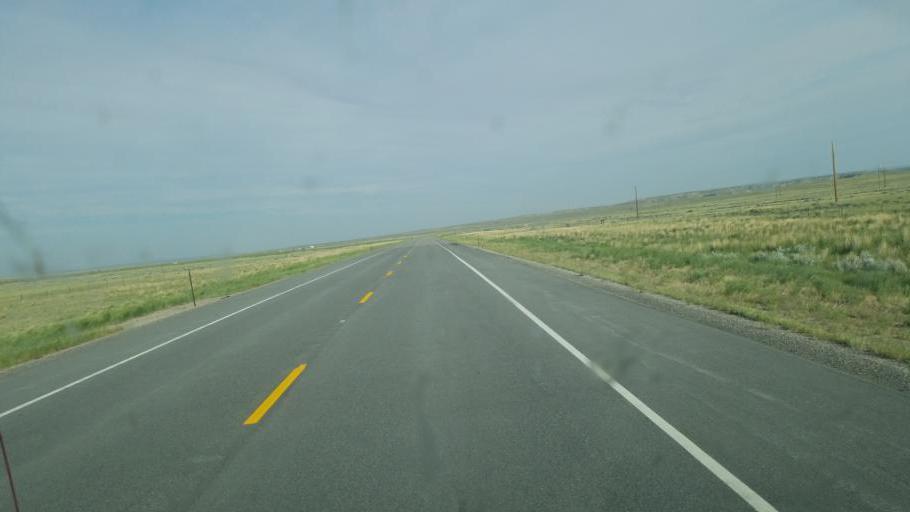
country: US
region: Wyoming
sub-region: Fremont County
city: Riverton
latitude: 43.1541
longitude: -107.6952
